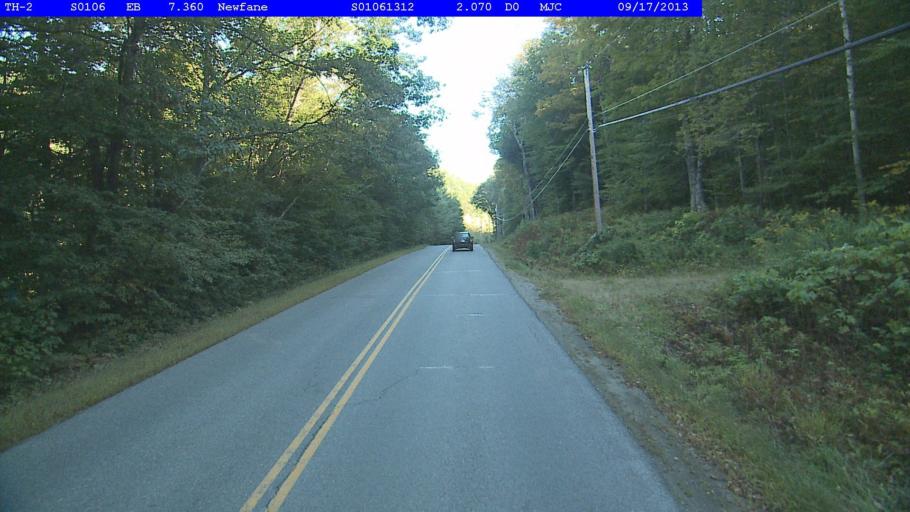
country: US
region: Vermont
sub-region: Windham County
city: Dover
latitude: 42.9455
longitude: -72.7301
